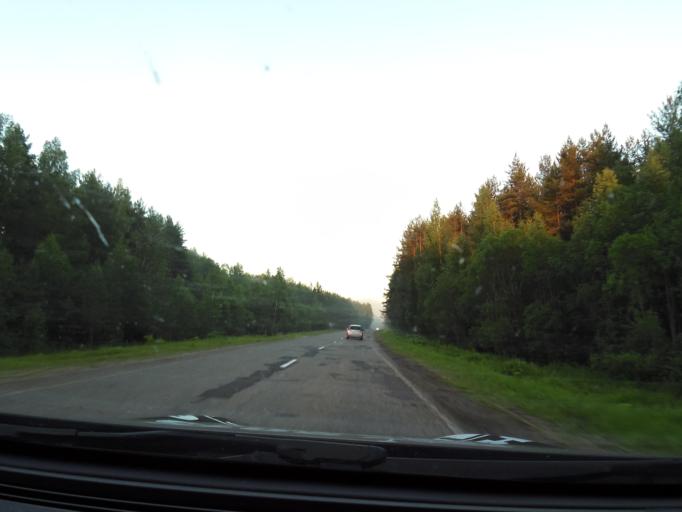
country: RU
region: Jaroslavl
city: Lyubim
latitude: 58.3656
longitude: 40.7570
